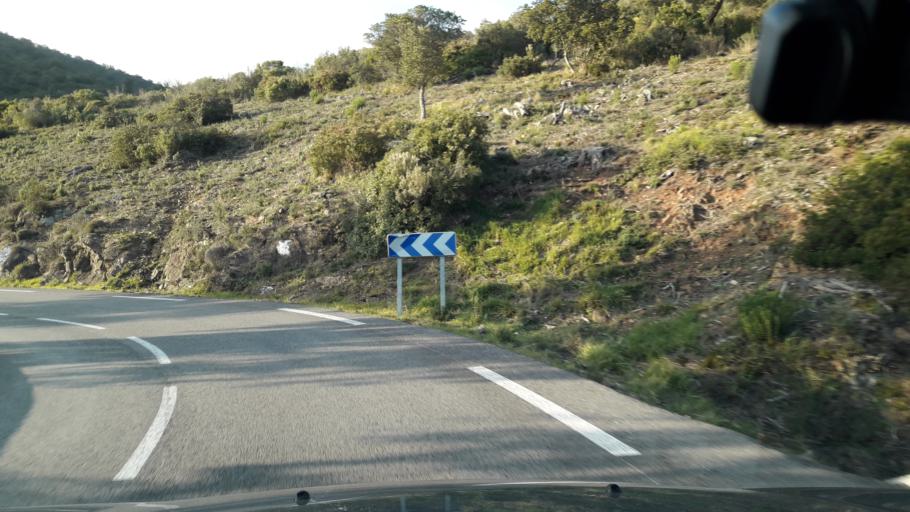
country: FR
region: Provence-Alpes-Cote d'Azur
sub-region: Departement du Var
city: Saint-Raphael
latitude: 43.5025
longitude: 6.7875
